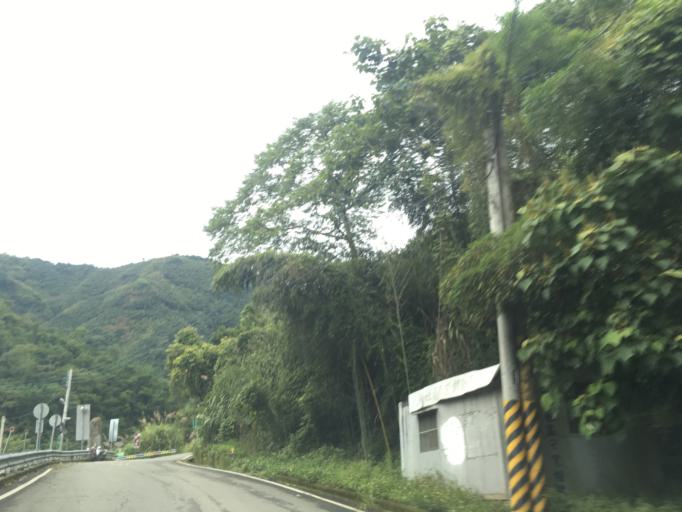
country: TW
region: Taiwan
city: Lugu
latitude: 23.5345
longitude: 120.7066
